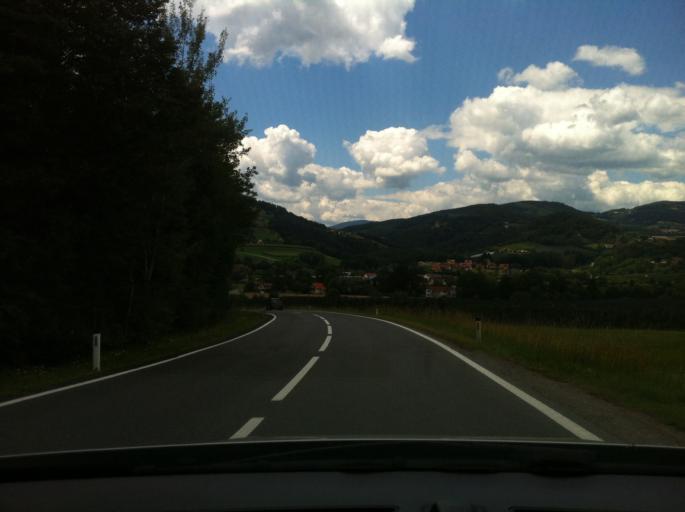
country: AT
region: Styria
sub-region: Politischer Bezirk Hartberg-Fuerstenfeld
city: Stubenberg
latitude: 47.2340
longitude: 15.8094
